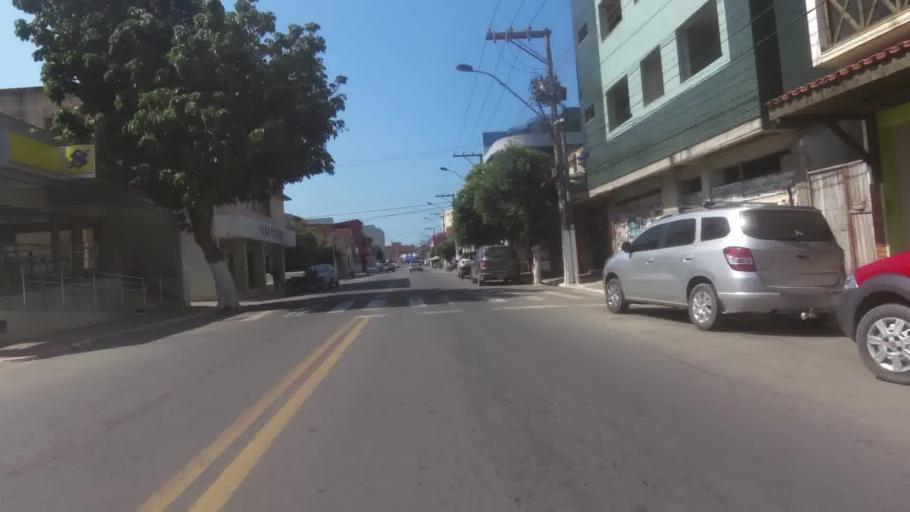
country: BR
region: Espirito Santo
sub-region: Marataizes
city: Marataizes
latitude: -21.0424
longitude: -40.8250
